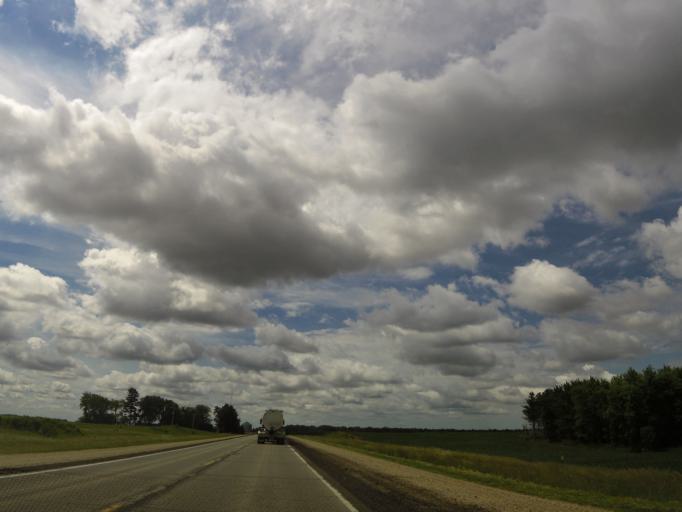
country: US
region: Iowa
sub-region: Howard County
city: Cresco
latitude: 43.2942
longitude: -92.2989
